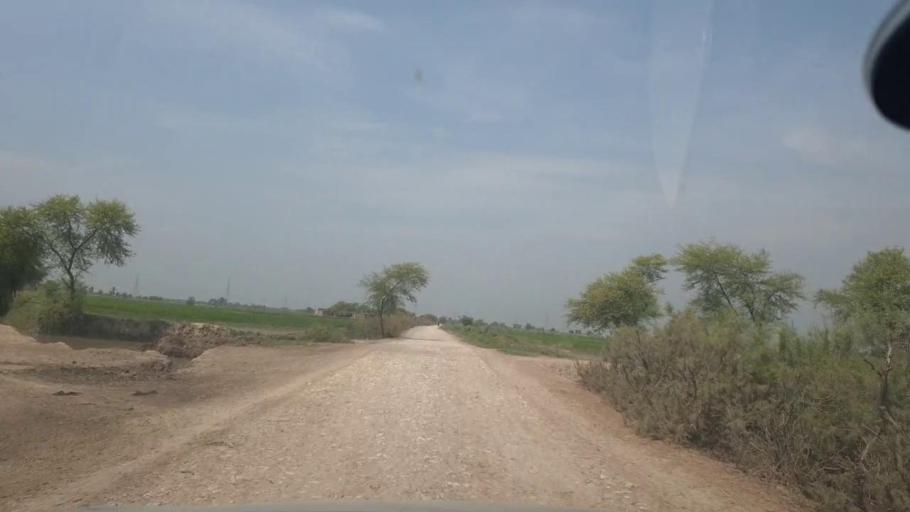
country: PK
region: Sindh
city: Thul
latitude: 28.1747
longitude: 68.6259
